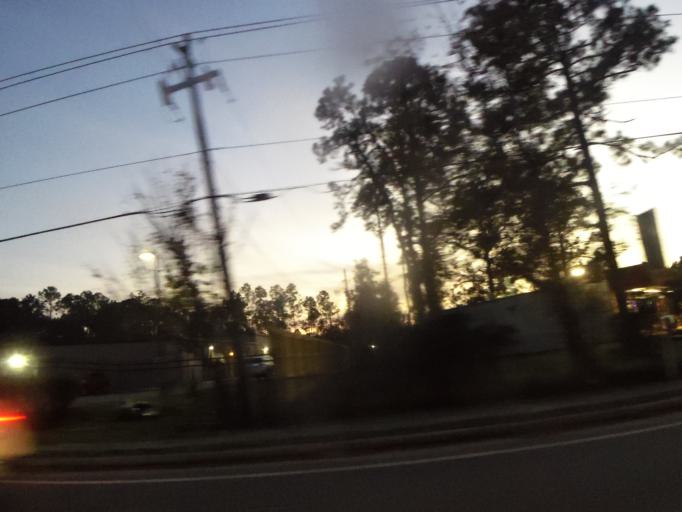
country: US
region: Florida
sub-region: Saint Johns County
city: Saint Augustine South
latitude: 29.8458
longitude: -81.3613
